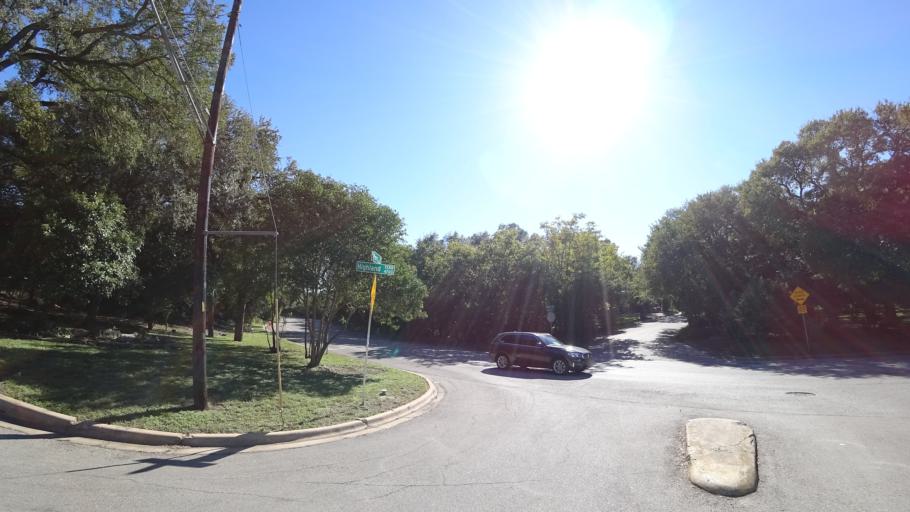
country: US
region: Texas
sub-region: Travis County
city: West Lake Hills
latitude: 30.3254
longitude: -97.7569
